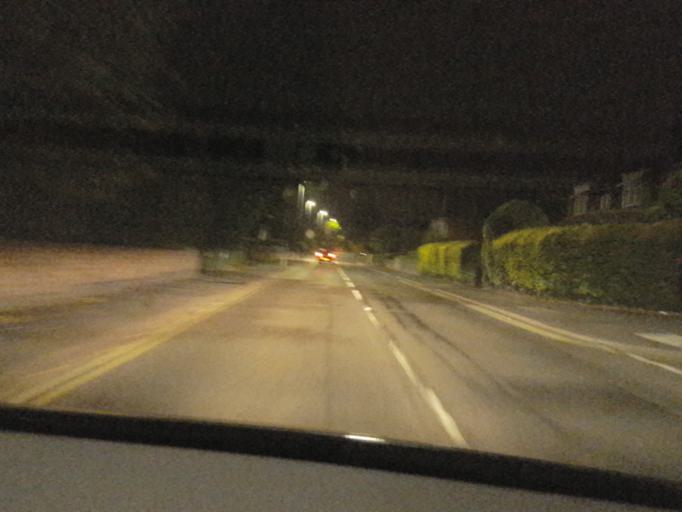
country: GB
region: England
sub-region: Leicestershire
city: Loughborough
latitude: 52.7616
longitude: -1.2259
